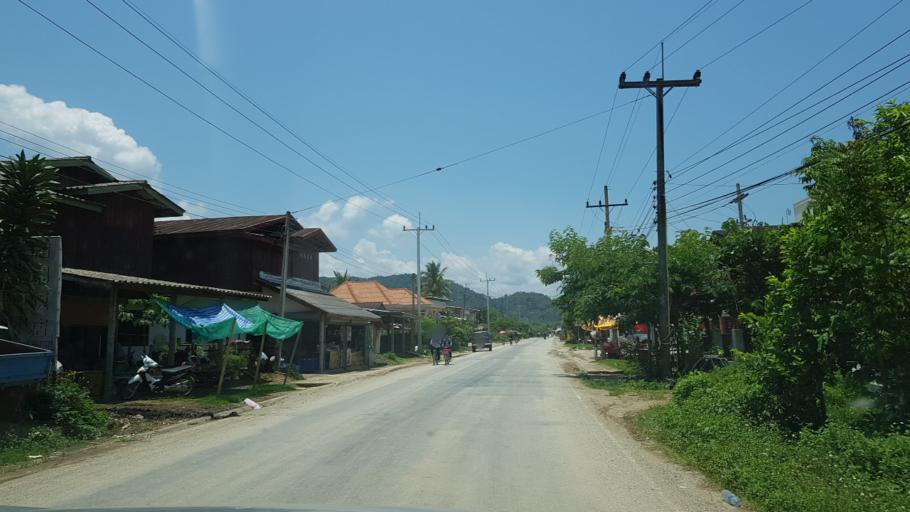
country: LA
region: Vientiane
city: Muang Kasi
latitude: 19.2319
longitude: 102.2529
